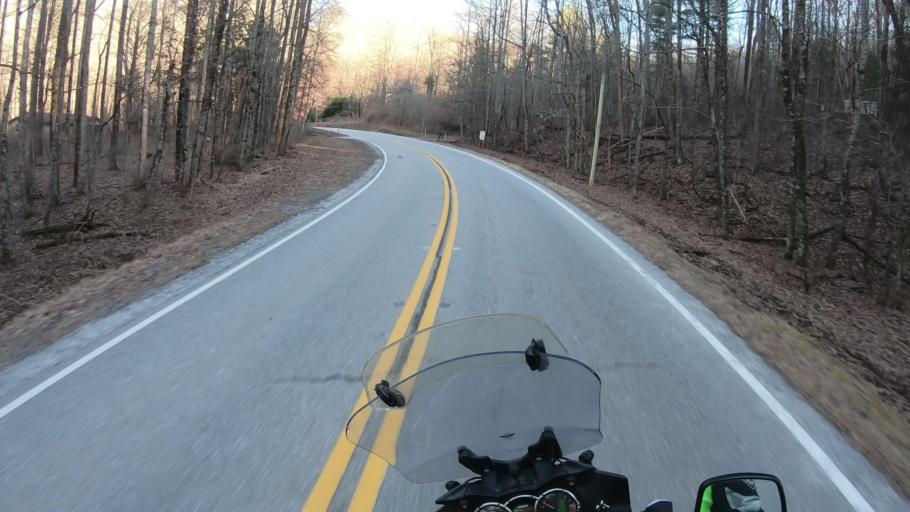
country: US
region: Georgia
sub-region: Lumpkin County
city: Dahlonega
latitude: 34.6889
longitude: -84.0150
